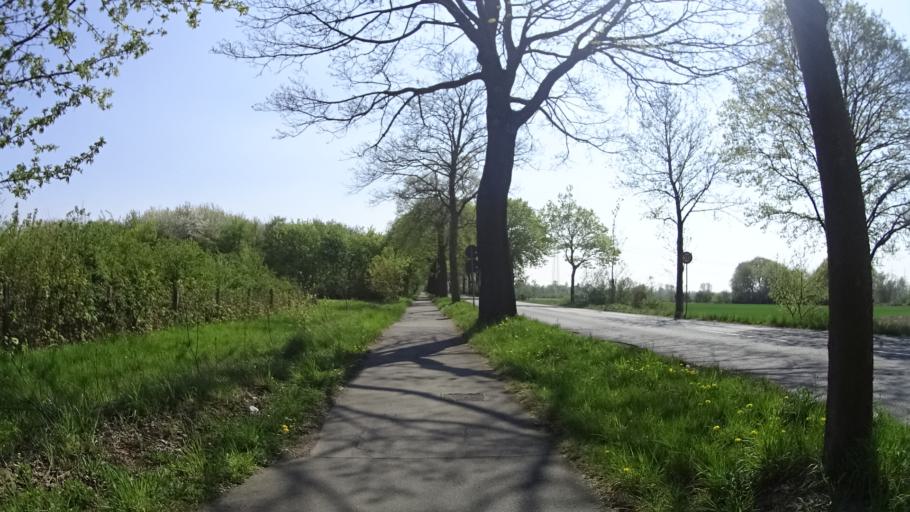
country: DE
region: North Rhine-Westphalia
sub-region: Regierungsbezirk Dusseldorf
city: Meerbusch
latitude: 51.3218
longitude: 6.6751
